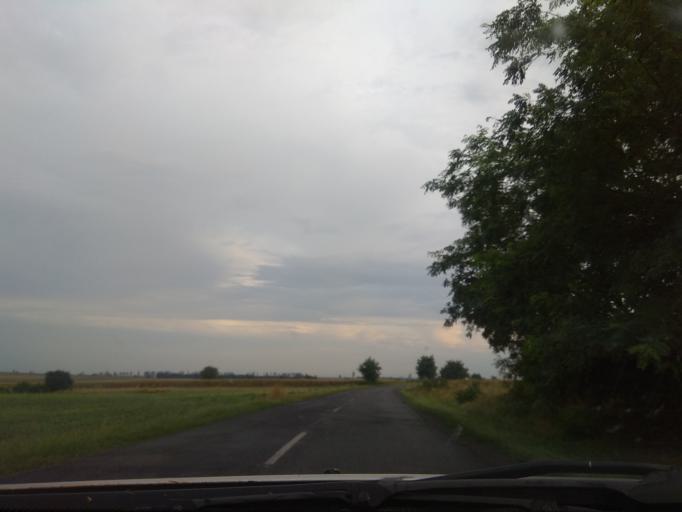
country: HU
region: Borsod-Abauj-Zemplen
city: Gesztely
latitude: 48.1226
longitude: 20.9733
